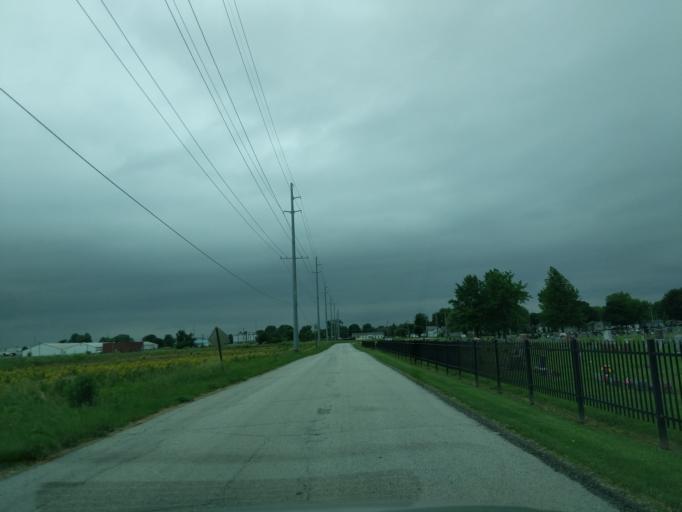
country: US
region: Indiana
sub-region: Tipton County
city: Tipton
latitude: 40.2772
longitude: -86.0505
